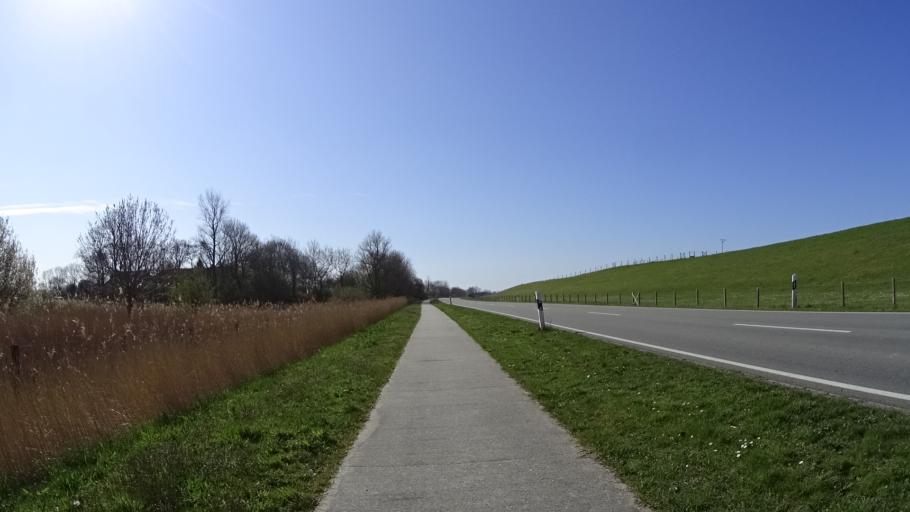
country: DE
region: Lower Saxony
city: Jemgum
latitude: 53.2727
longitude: 7.4076
